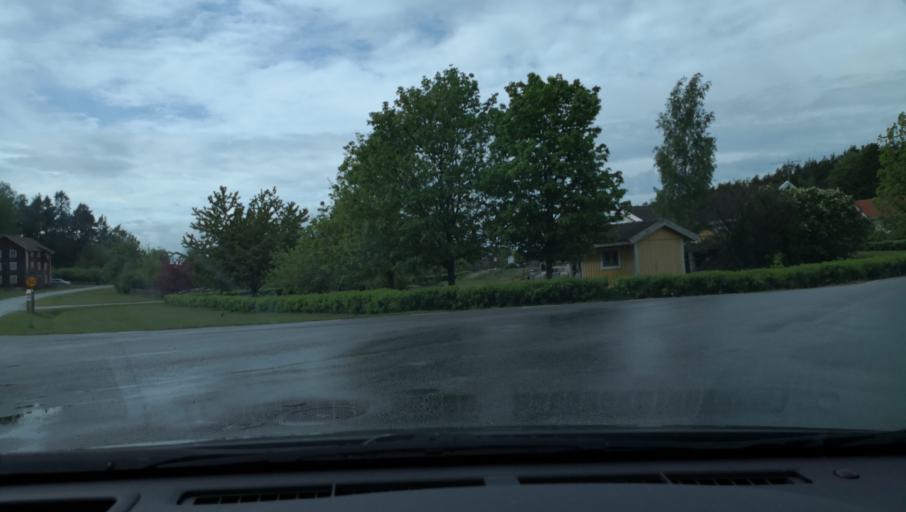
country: SE
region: Uppsala
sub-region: Enkopings Kommun
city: Orsundsbro
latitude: 59.6887
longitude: 17.3764
